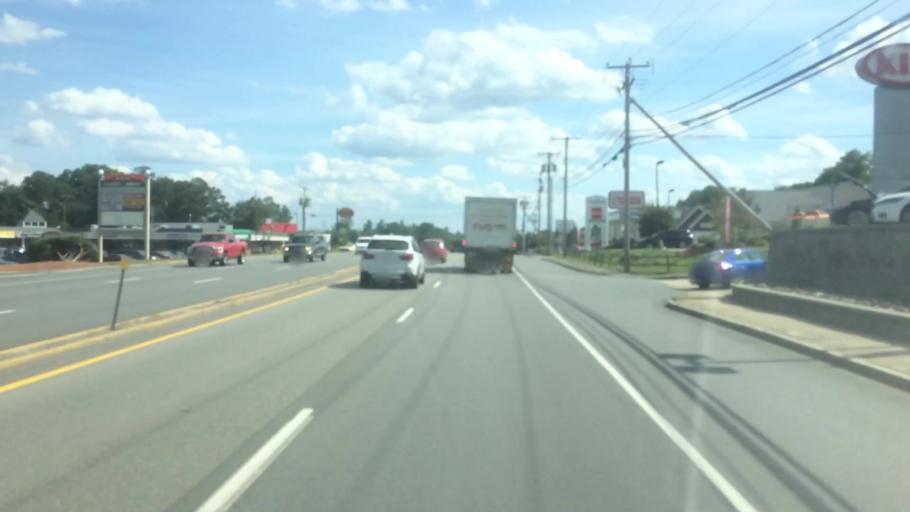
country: US
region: New Hampshire
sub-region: Hillsborough County
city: Hudson
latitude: 42.7292
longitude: -71.4486
